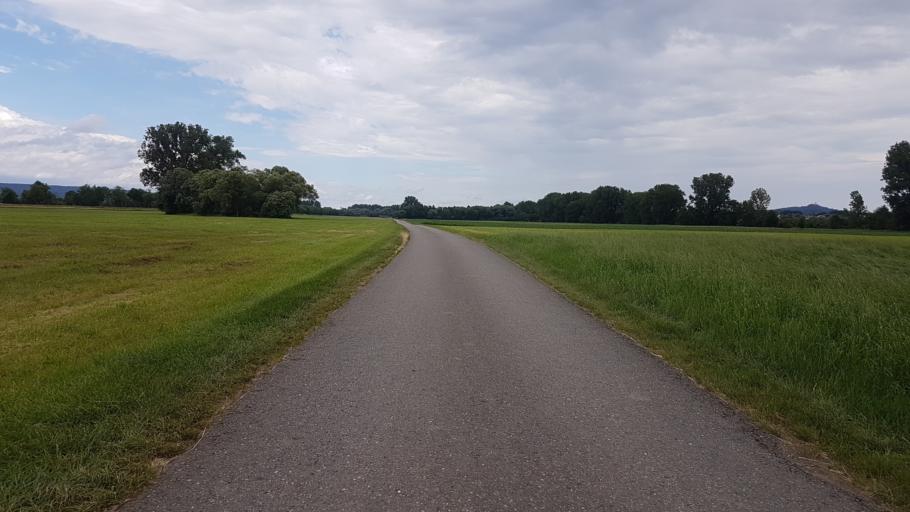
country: DE
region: Baden-Wuerttemberg
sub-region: Tuebingen Region
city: Neufra
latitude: 48.1204
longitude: 9.4554
